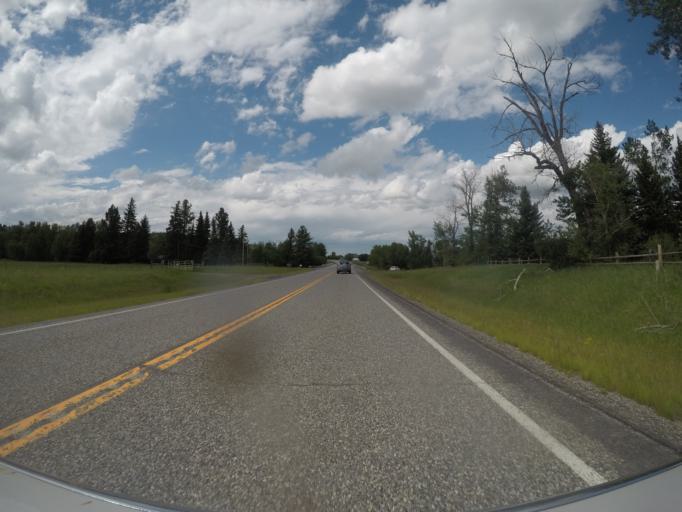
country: US
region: Montana
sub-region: Sweet Grass County
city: Big Timber
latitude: 45.7221
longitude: -109.9969
